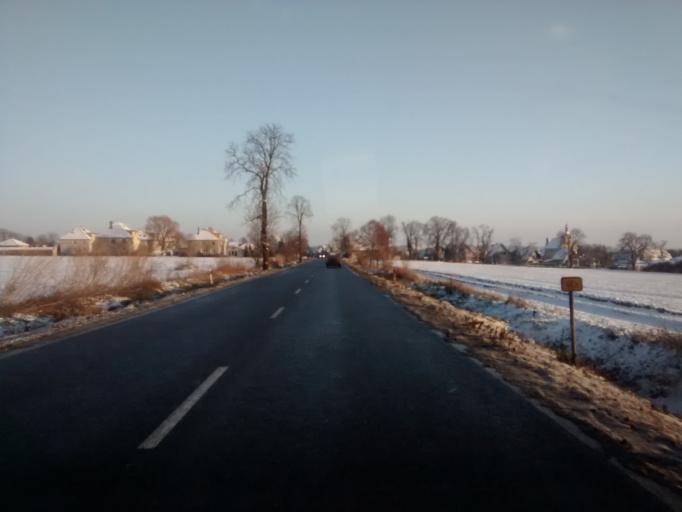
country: CZ
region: Central Bohemia
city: Bysice
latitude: 50.3148
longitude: 14.5845
